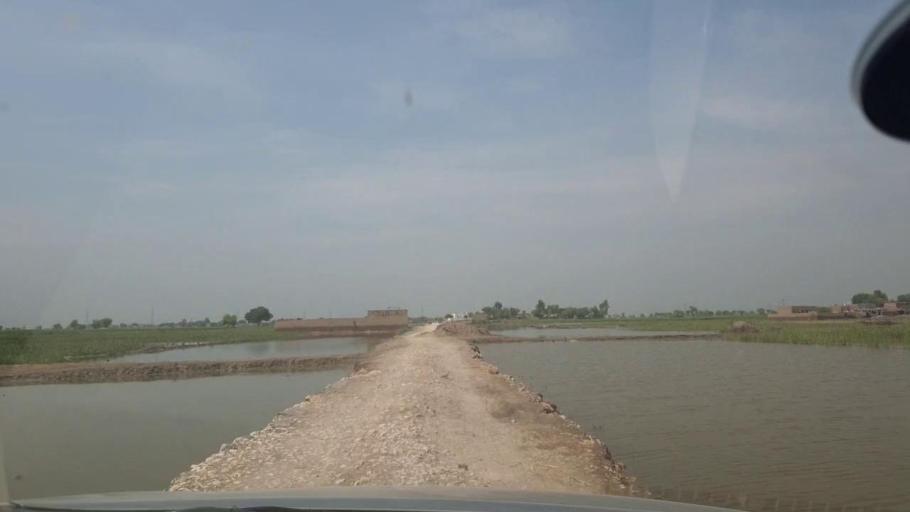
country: PK
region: Sindh
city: Thul
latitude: 28.1712
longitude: 68.6312
